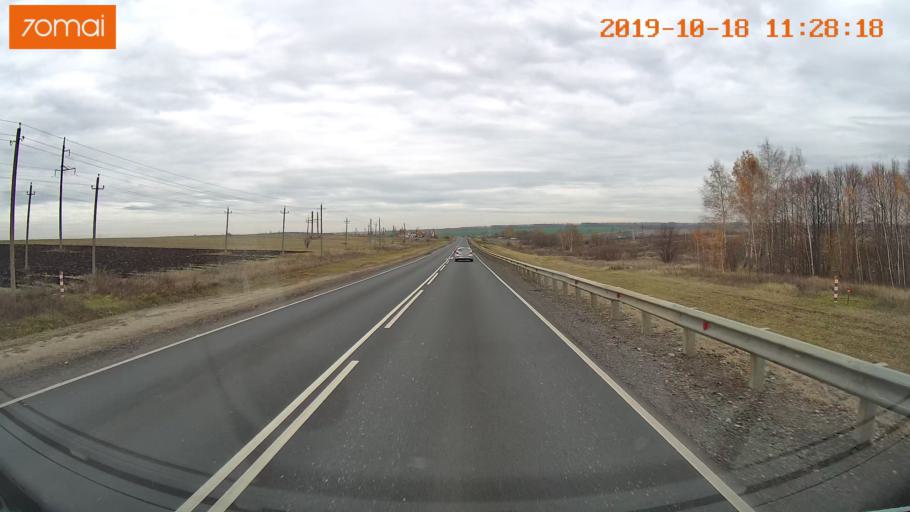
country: RU
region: Tula
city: Kimovsk
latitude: 54.1532
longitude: 38.6582
